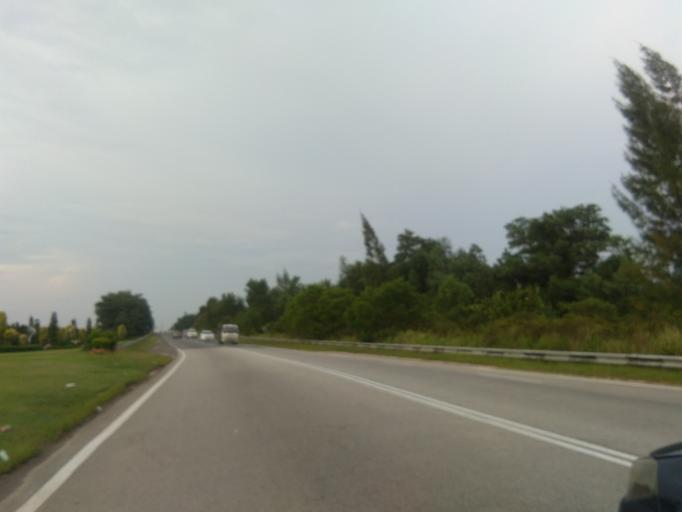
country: MY
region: Penang
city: Tasek Glugor
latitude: 5.5086
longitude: 100.6251
